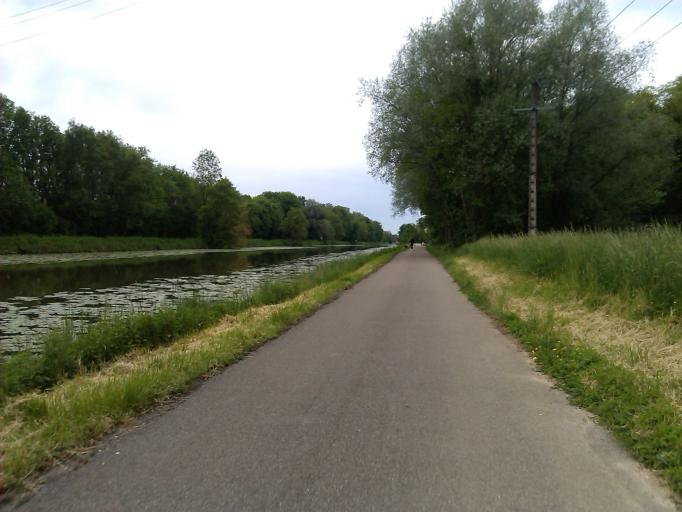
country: FR
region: Franche-Comte
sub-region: Departement du Jura
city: Choisey
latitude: 47.0715
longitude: 5.4690
